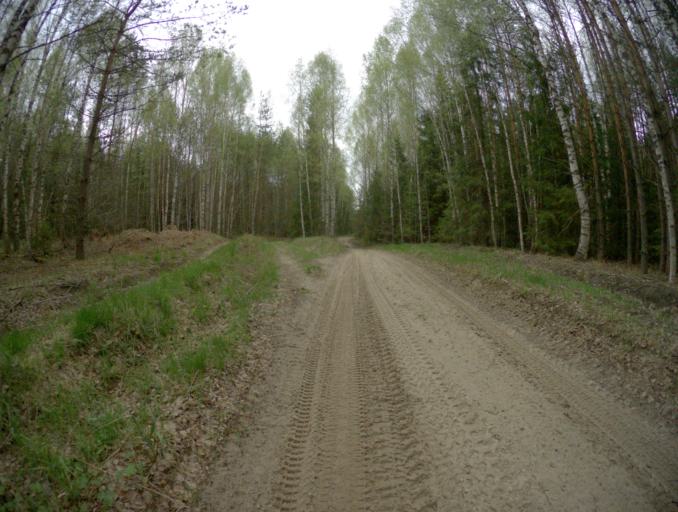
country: RU
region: Vladimir
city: Golovino
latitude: 55.8881
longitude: 40.4082
